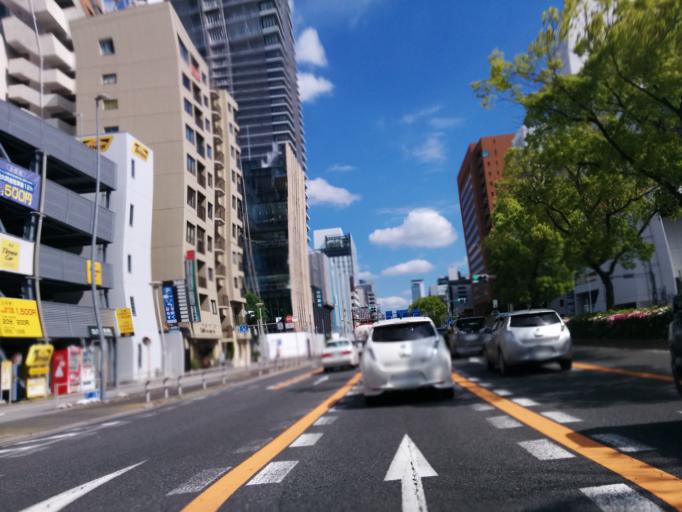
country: JP
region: Aichi
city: Nagoya-shi
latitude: 35.1656
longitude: 136.8977
